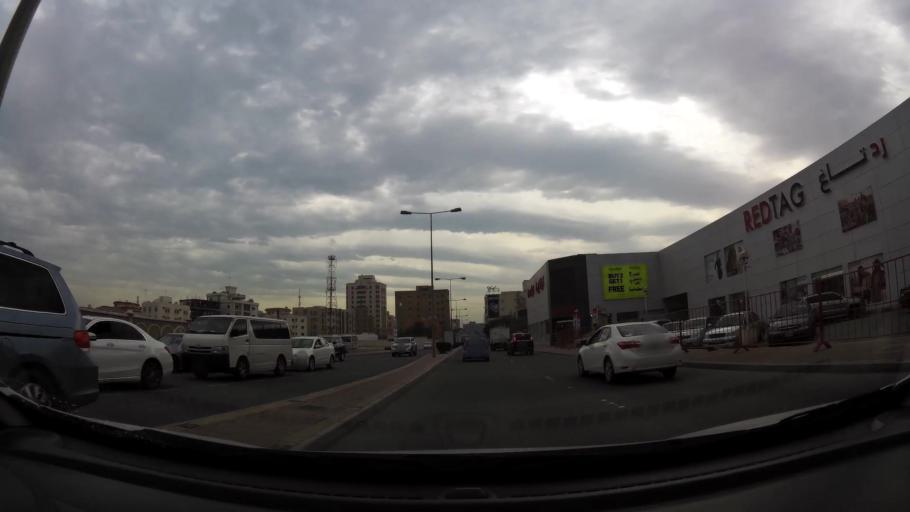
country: BH
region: Manama
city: Manama
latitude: 26.2206
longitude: 50.5851
